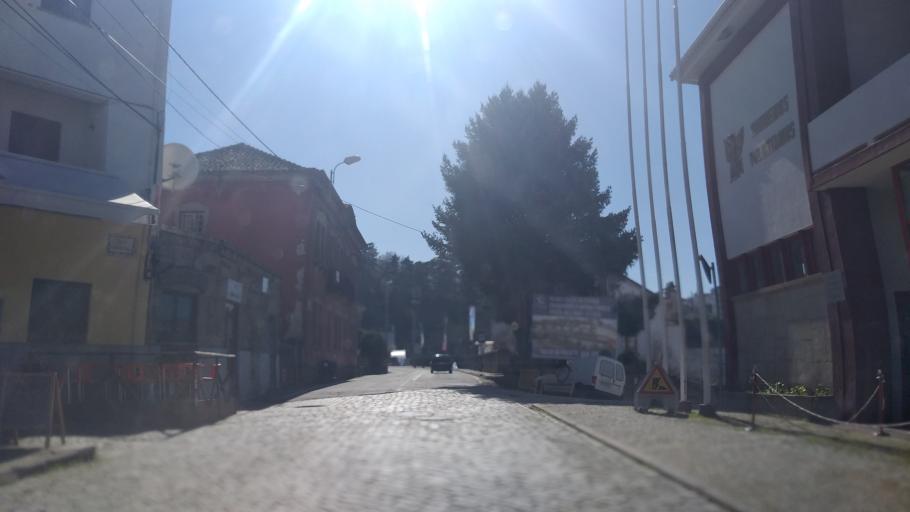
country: PT
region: Guarda
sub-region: Manteigas
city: Manteigas
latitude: 40.4920
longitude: -7.5929
